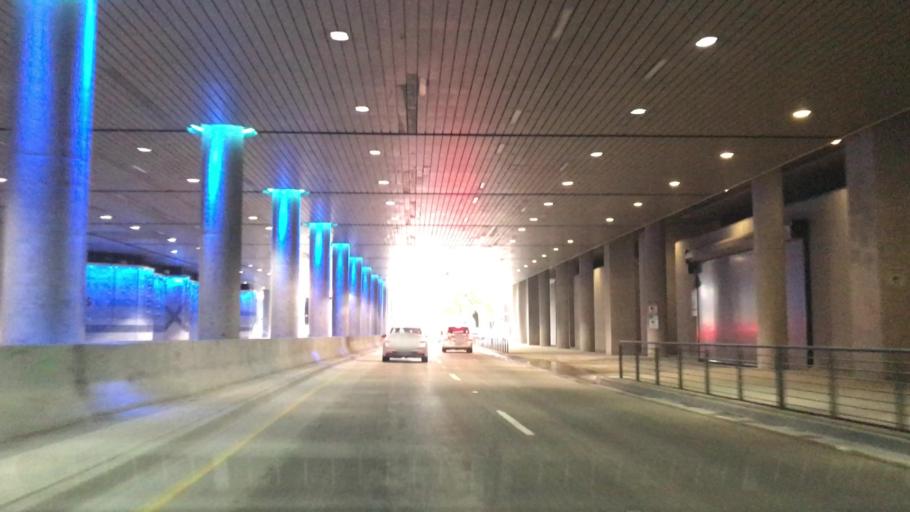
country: US
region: Texas
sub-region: Dallas County
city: Dallas
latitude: 32.7733
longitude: -96.8024
